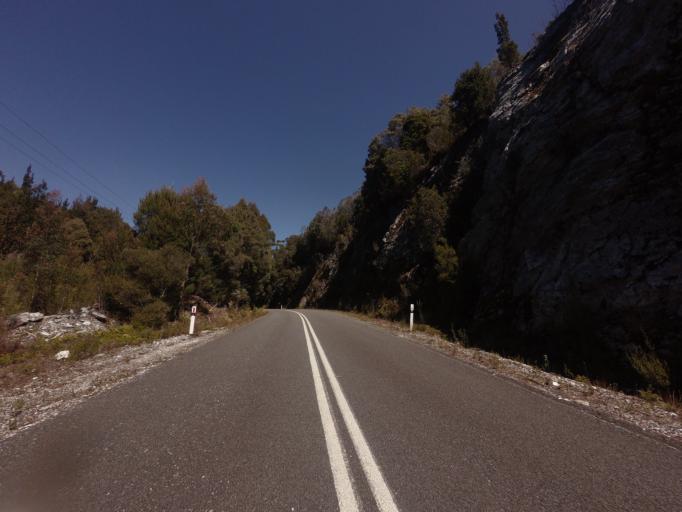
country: AU
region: Tasmania
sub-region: West Coast
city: Queenstown
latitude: -42.7582
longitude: 146.0031
